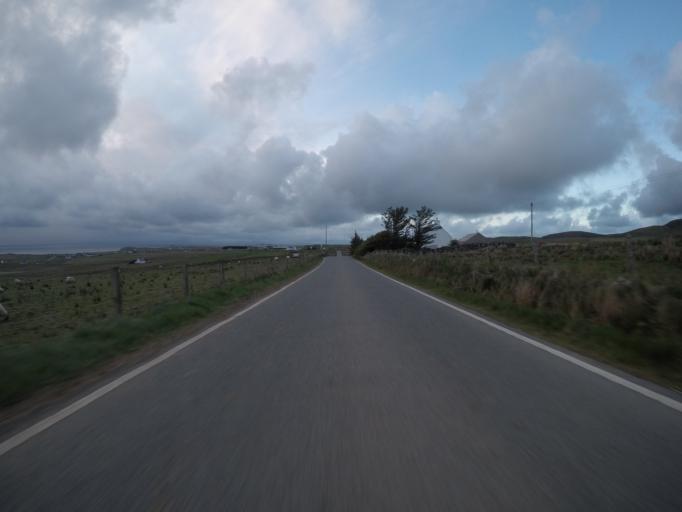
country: GB
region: Scotland
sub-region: Highland
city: Portree
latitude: 57.6388
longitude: -6.3765
